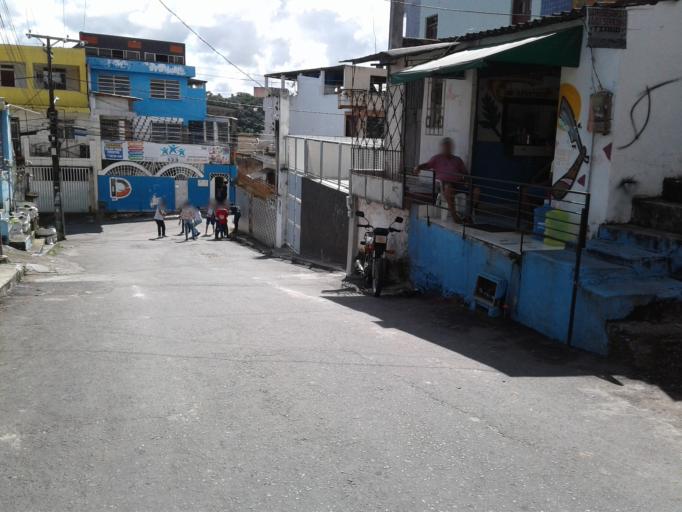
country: BR
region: Bahia
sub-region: Salvador
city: Salvador
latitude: -12.9125
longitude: -38.4699
